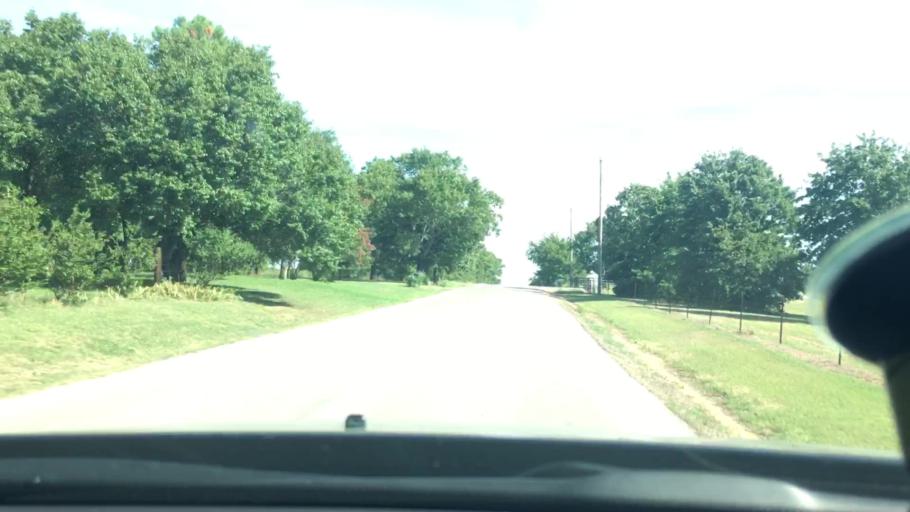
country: US
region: Oklahoma
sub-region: Carter County
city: Lone Grove
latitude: 34.2735
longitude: -97.2824
